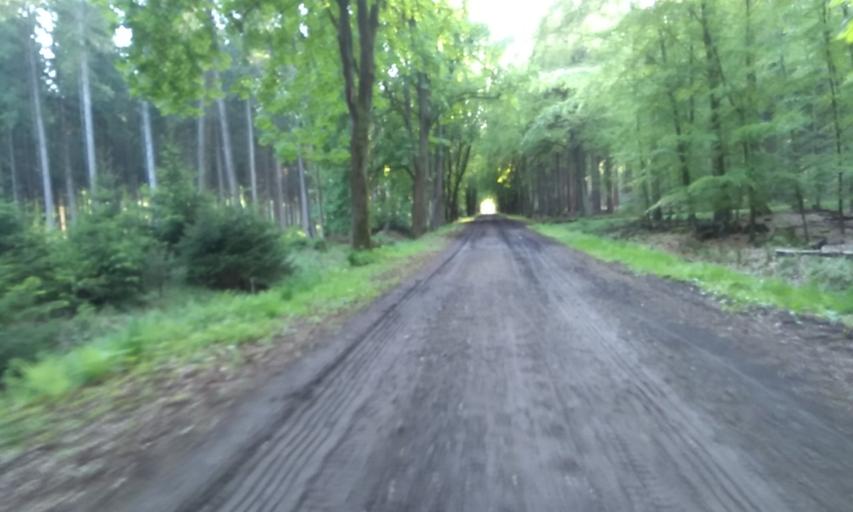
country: DE
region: Lower Saxony
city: Wohnste
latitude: 53.3921
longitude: 9.5312
